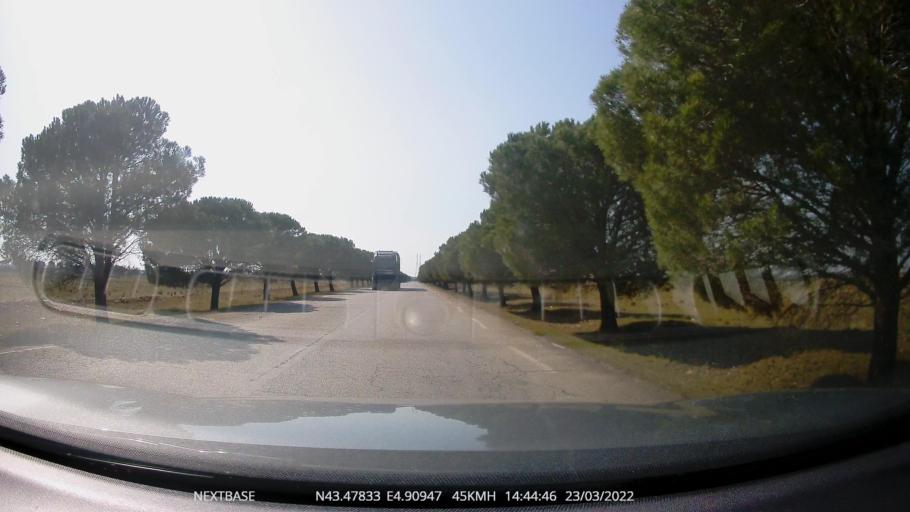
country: FR
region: Provence-Alpes-Cote d'Azur
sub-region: Departement des Bouches-du-Rhone
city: Fos-sur-Mer
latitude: 43.4783
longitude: 4.9094
